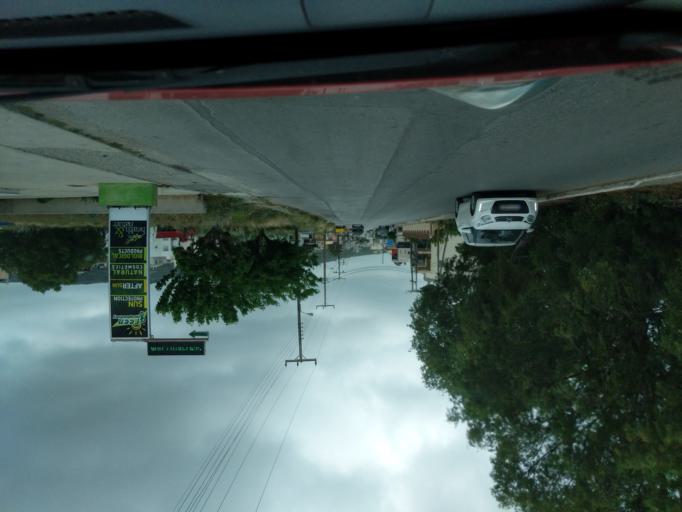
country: GR
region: Crete
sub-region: Nomos Chanias
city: Kissamos
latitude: 35.4985
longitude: 23.6463
